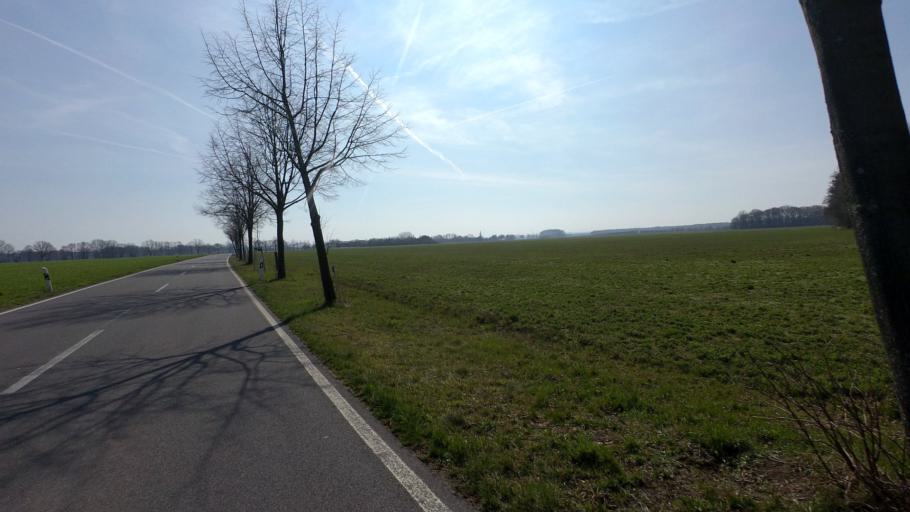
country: DE
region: Brandenburg
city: Golssen
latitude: 51.9488
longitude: 13.5978
